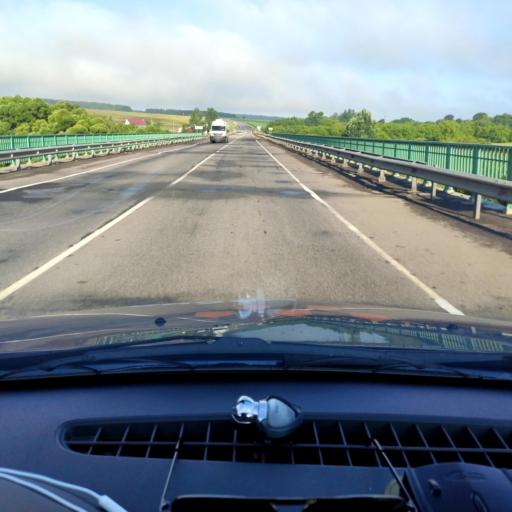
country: RU
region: Orjol
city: Livny
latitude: 52.4478
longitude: 37.4713
